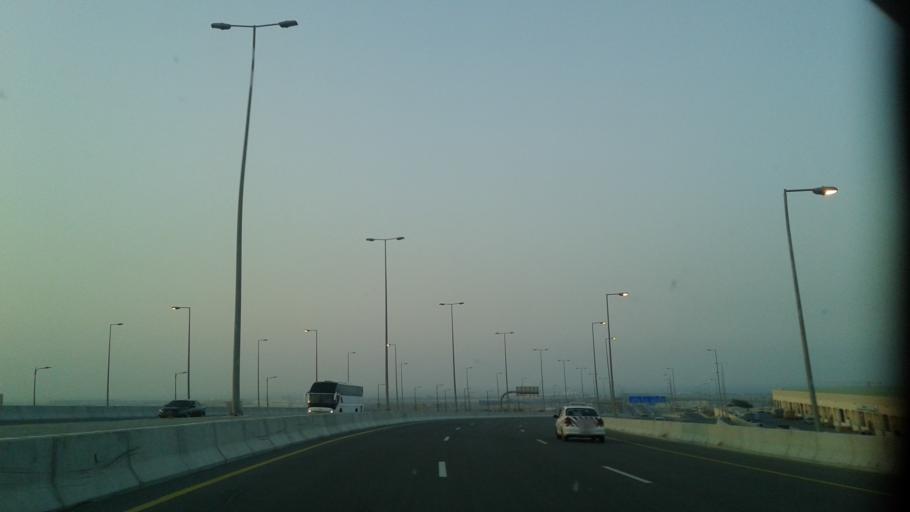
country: OM
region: Muhafazat Masqat
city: Bawshar
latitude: 23.5712
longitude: 58.3330
